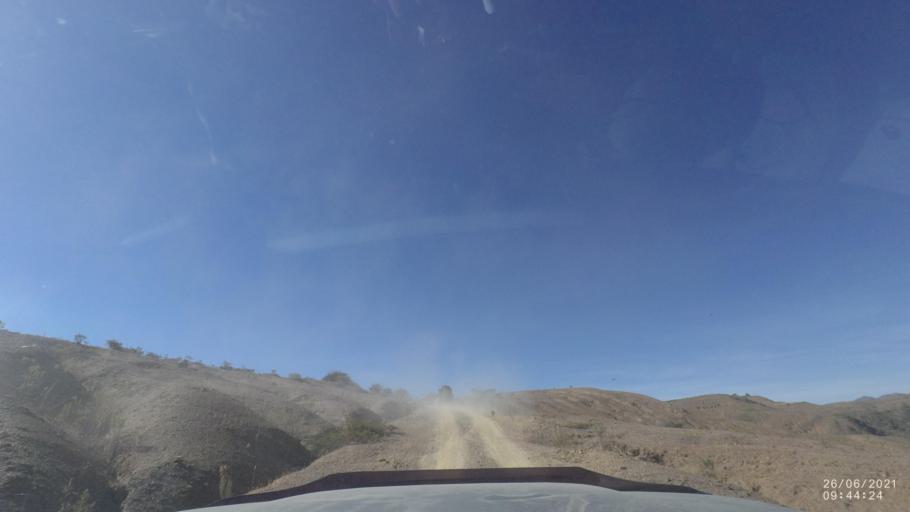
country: BO
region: Cochabamba
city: Mizque
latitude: -17.9451
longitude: -65.6331
